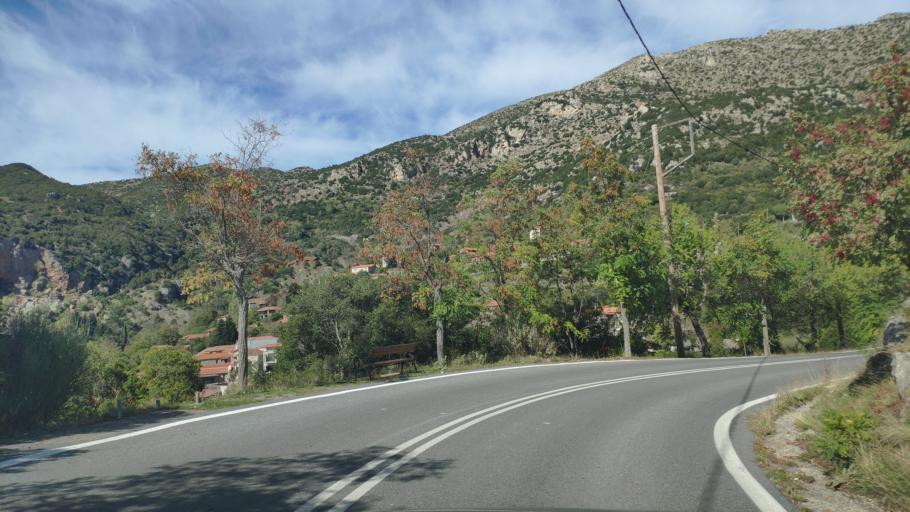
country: GR
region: Peloponnese
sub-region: Nomos Arkadias
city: Dimitsana
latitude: 37.5537
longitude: 22.0847
